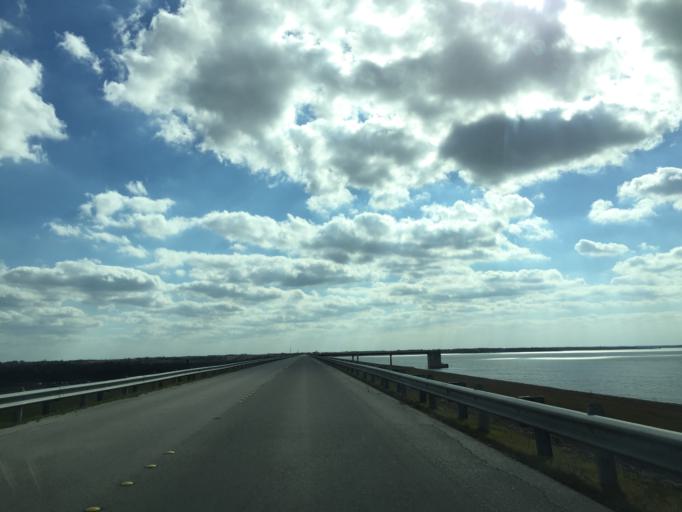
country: US
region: Texas
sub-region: Williamson County
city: Granger
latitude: 30.7063
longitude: -97.3276
